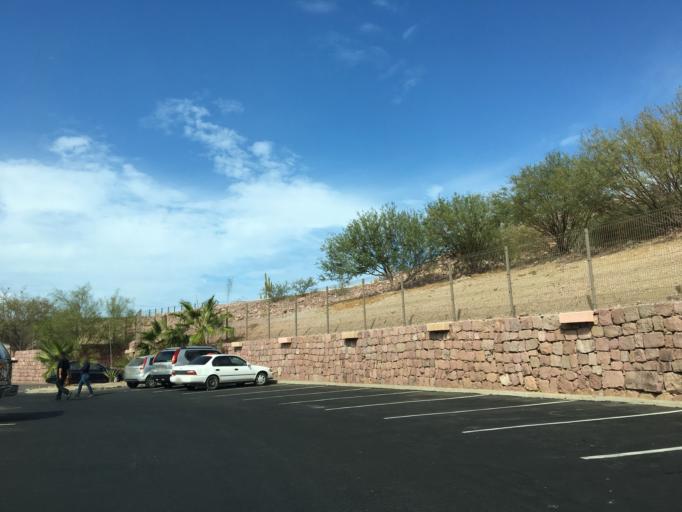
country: MX
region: Baja California Sur
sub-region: La Paz
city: La Paz
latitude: 24.2150
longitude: -110.2976
